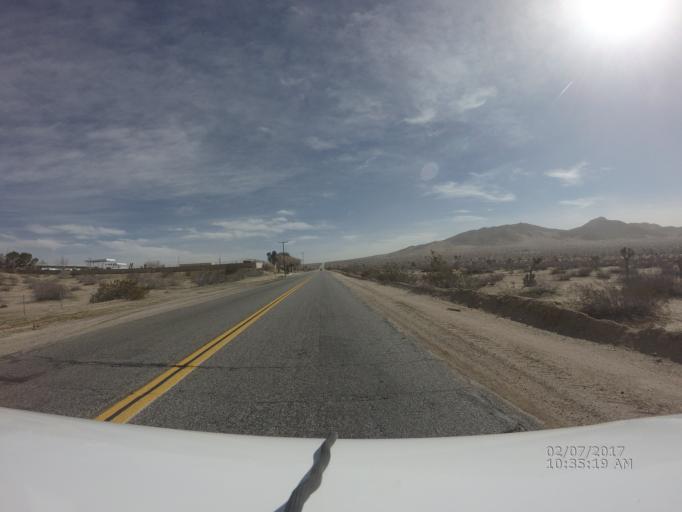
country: US
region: California
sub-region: Los Angeles County
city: Lake Los Angeles
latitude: 34.6900
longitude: -117.8199
